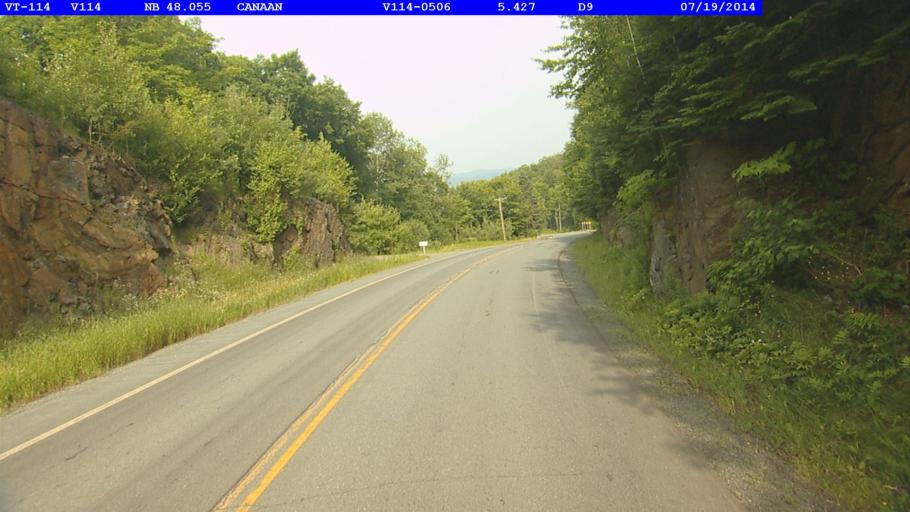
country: US
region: New Hampshire
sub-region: Coos County
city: Colebrook
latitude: 45.0092
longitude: -71.5871
